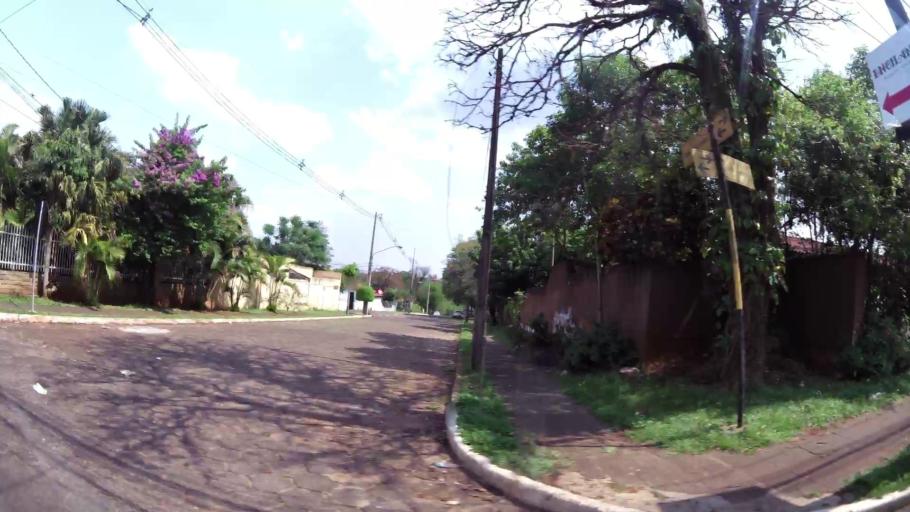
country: PY
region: Alto Parana
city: Ciudad del Este
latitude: -25.5125
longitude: -54.6395
